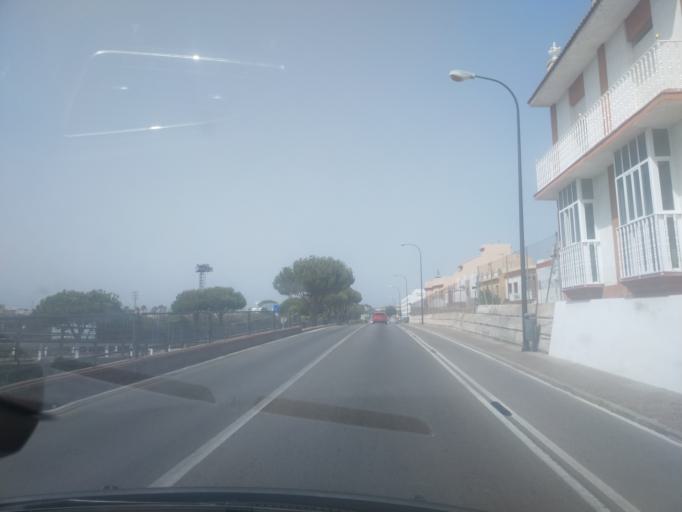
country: ES
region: Andalusia
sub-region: Provincia de Cadiz
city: San Fernando
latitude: 36.4645
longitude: -6.2081
